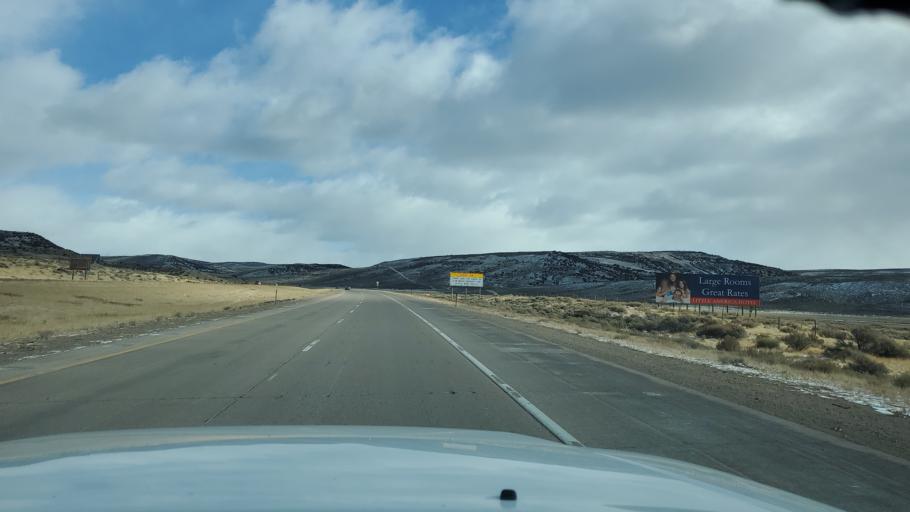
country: US
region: Wyoming
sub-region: Uinta County
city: Evanston
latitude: 41.2623
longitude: -110.8861
